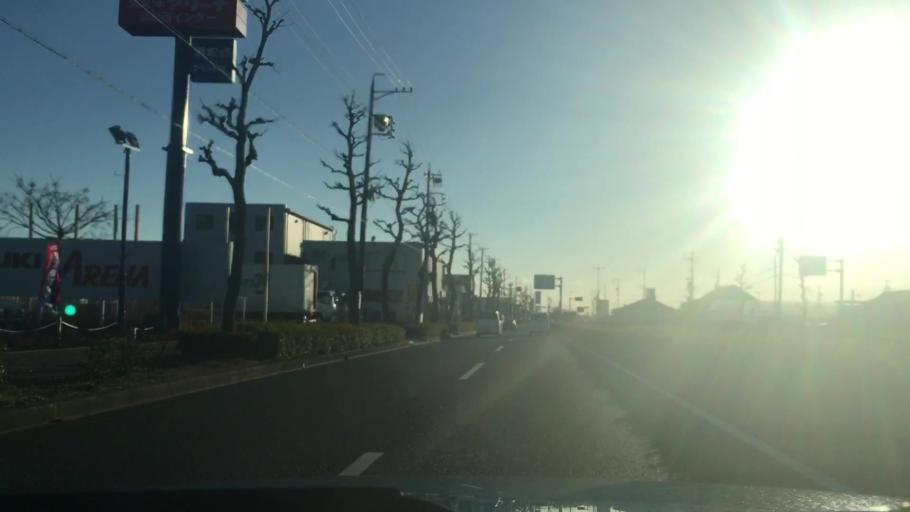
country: JP
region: Shizuoka
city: Hamamatsu
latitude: 34.7593
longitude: 137.6801
